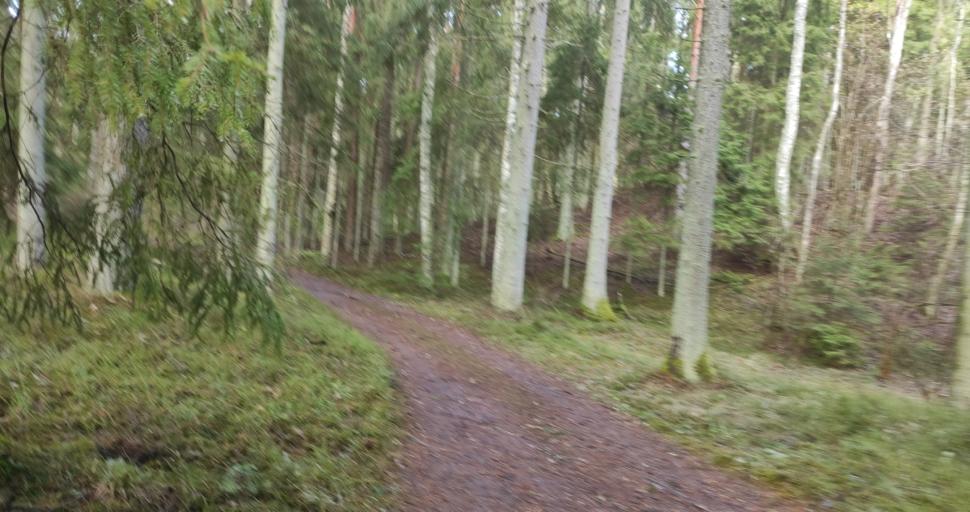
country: LV
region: Tukuma Rajons
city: Tukums
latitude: 57.1129
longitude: 23.0410
